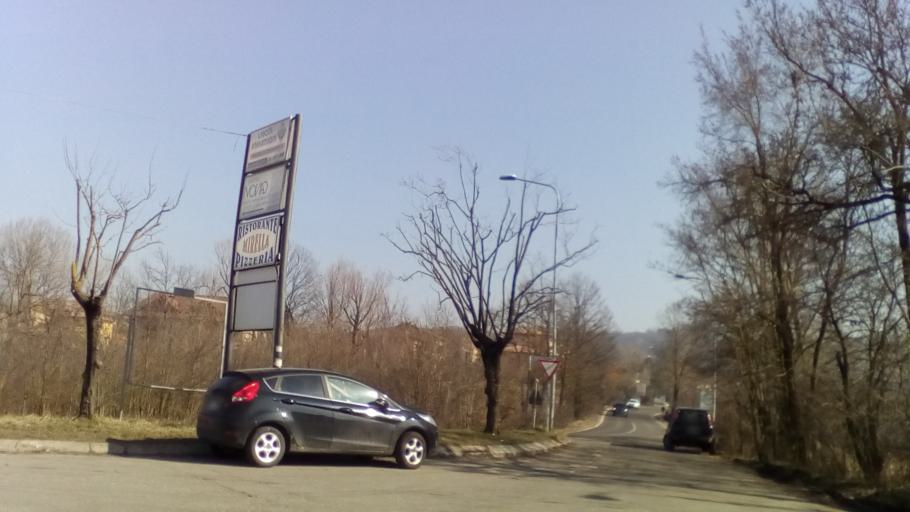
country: IT
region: Emilia-Romagna
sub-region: Provincia di Modena
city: Sant'Antonio
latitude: 44.3647
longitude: 10.8345
